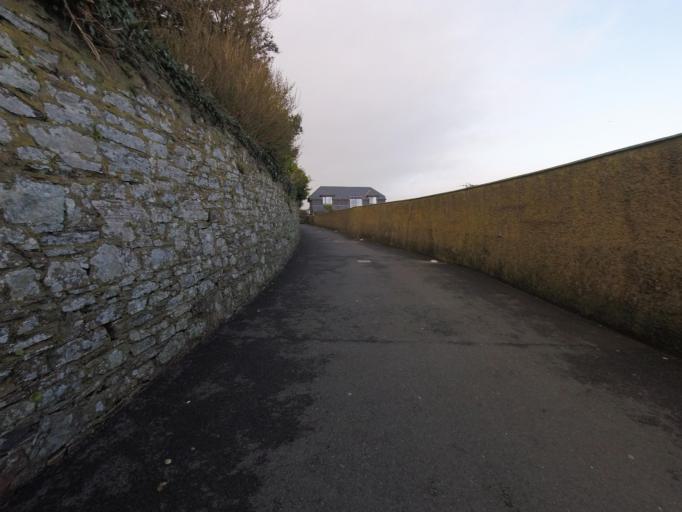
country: IE
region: Munster
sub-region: Waterford
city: Tra Mhor
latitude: 52.1576
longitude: -7.1540
